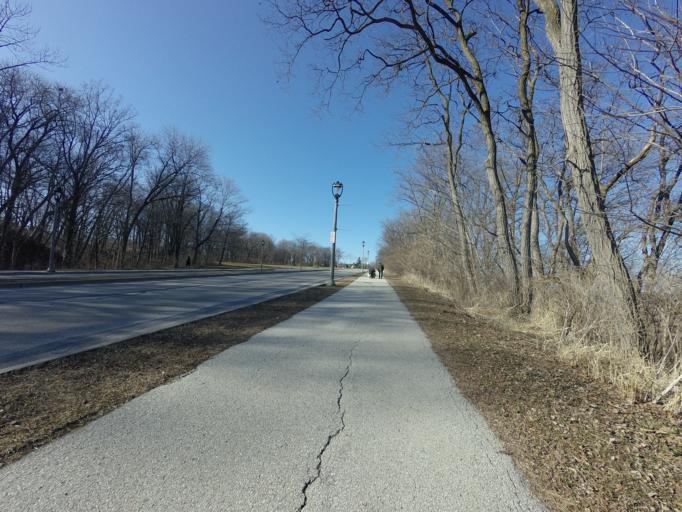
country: US
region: Wisconsin
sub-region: Milwaukee County
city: Shorewood
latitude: 43.0717
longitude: -87.8672
